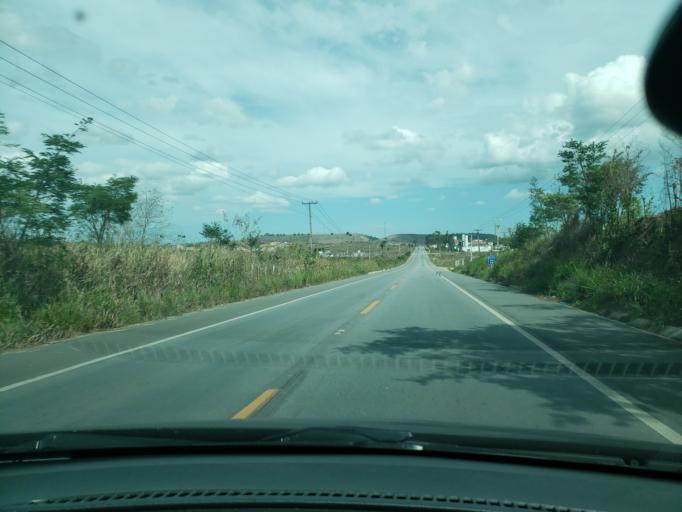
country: BR
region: Alagoas
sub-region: Murici
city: Murici
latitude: -9.3025
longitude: -35.9498
